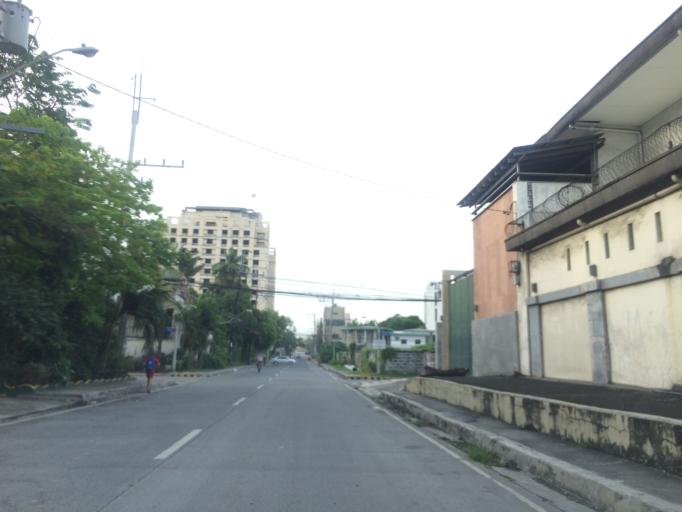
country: PH
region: Calabarzon
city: Del Monte
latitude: 14.6335
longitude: 121.0042
